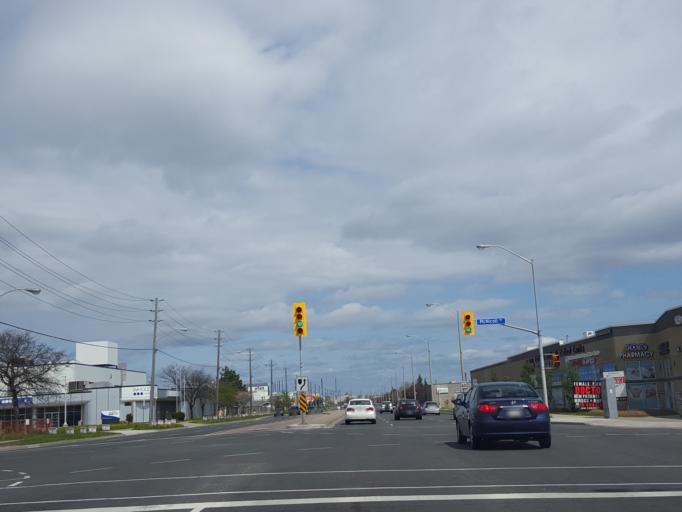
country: CA
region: Ontario
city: Markham
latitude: 43.8238
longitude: -79.2477
